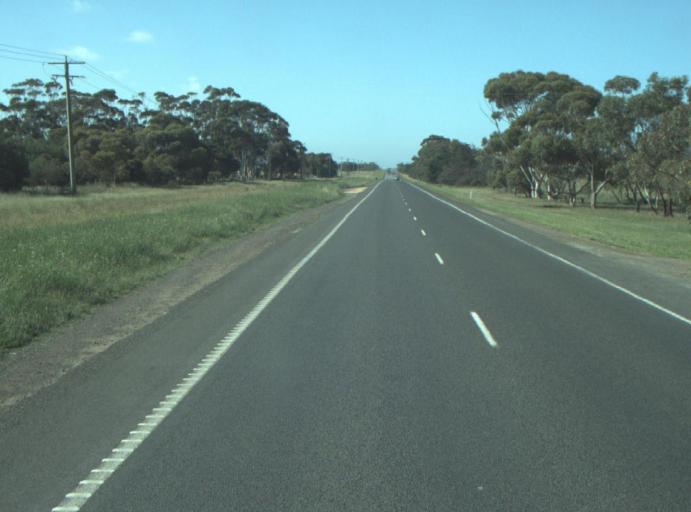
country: AU
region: Victoria
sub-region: Greater Geelong
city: Lara
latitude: -38.0034
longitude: 144.3493
